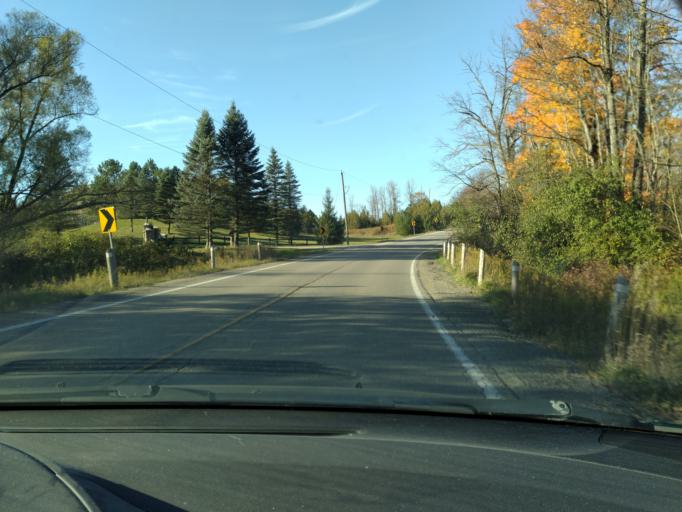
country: CA
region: Ontario
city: Vaughan
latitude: 43.9058
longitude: -79.7078
